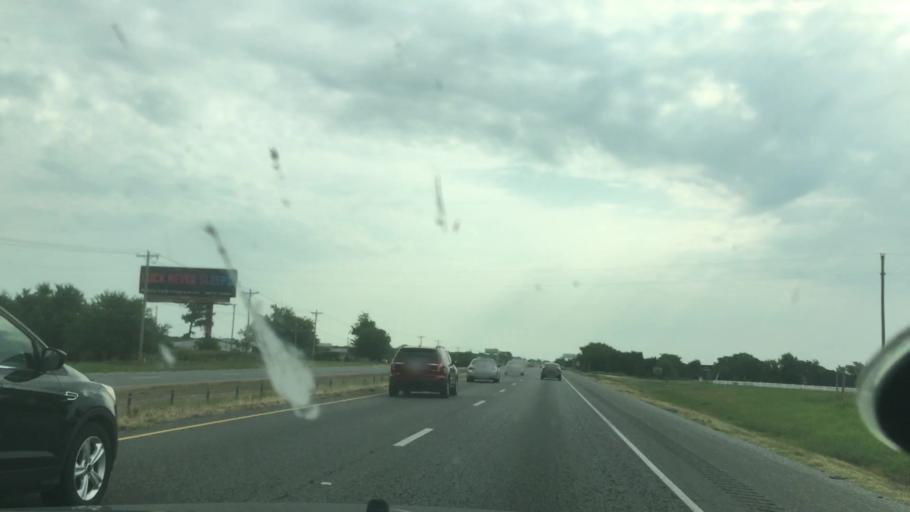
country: US
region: Oklahoma
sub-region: Bryan County
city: Colbert
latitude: 33.8827
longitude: -96.4936
